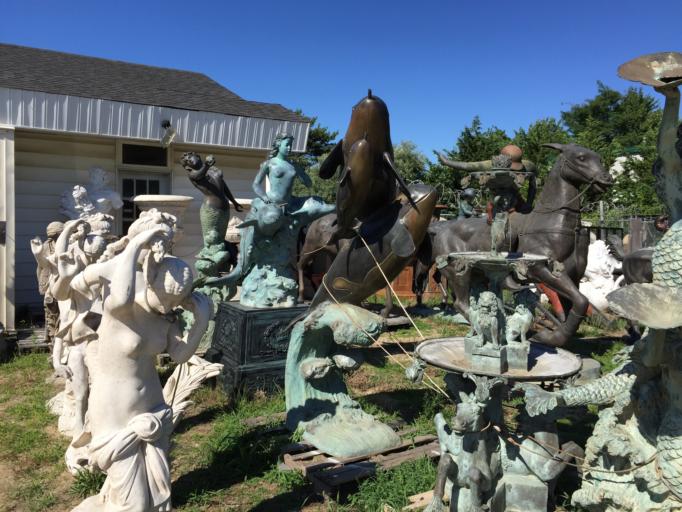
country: US
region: New York
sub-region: Suffolk County
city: Shinnecock Hills
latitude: 40.8951
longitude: -72.4503
